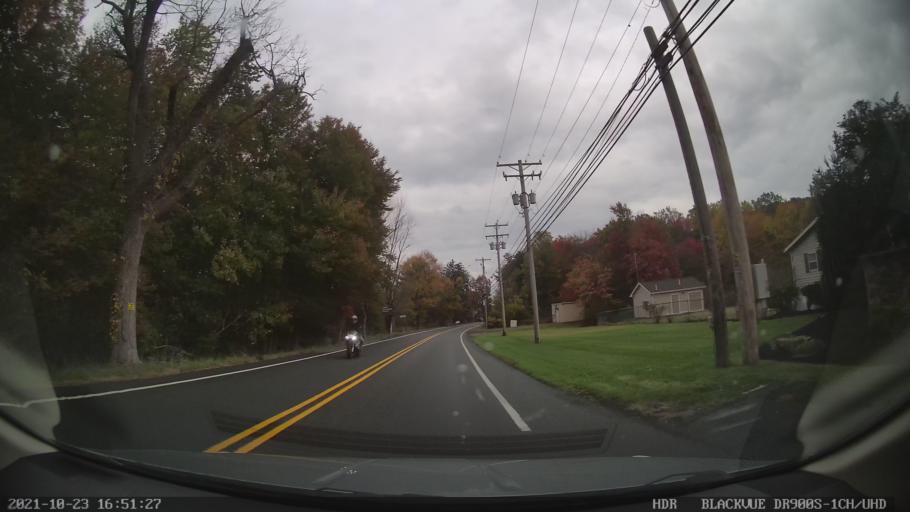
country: US
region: Pennsylvania
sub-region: Berks County
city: Red Lion
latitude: 40.4719
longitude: -75.6073
